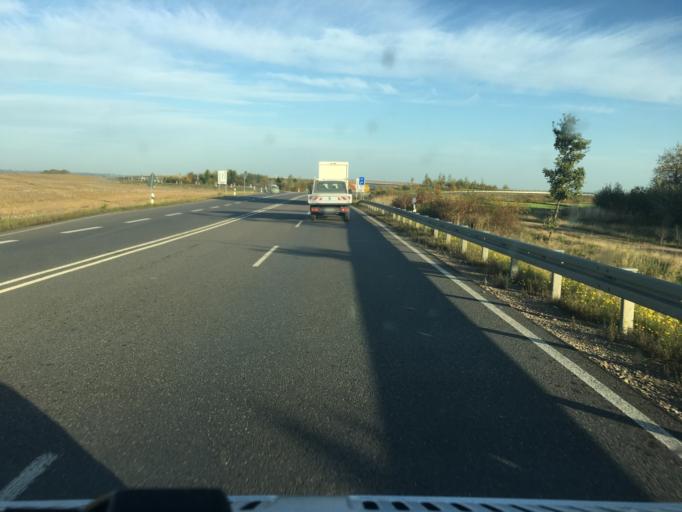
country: DE
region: Saxony
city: Lichtentanne
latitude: 50.6668
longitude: 12.4442
